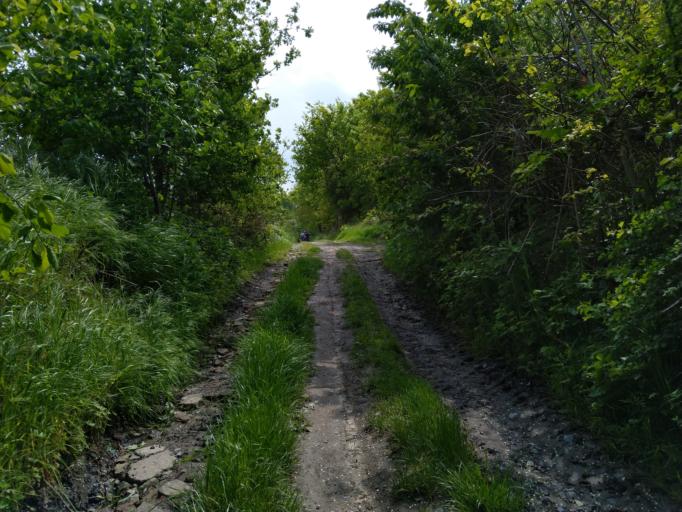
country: BE
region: Wallonia
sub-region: Province du Hainaut
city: Mons
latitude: 50.4418
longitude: 3.9832
